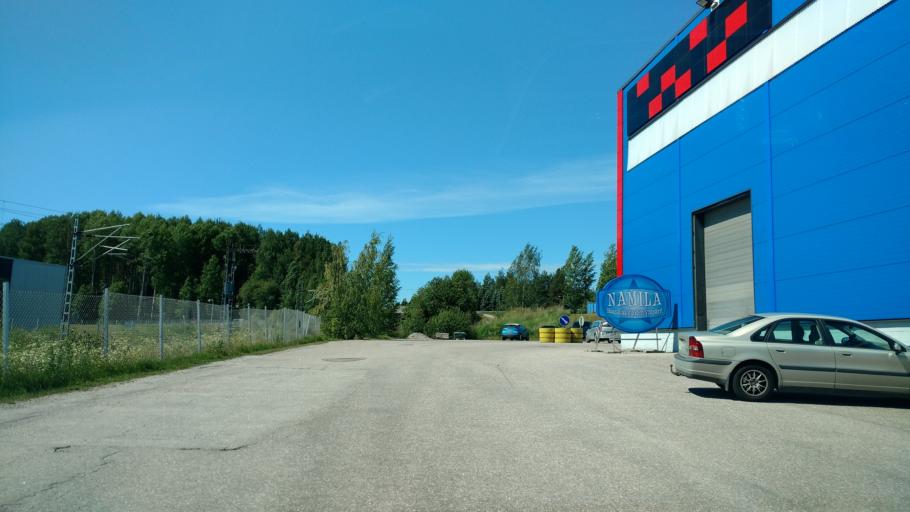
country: FI
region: Varsinais-Suomi
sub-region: Salo
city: Halikko
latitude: 60.3914
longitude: 23.1078
